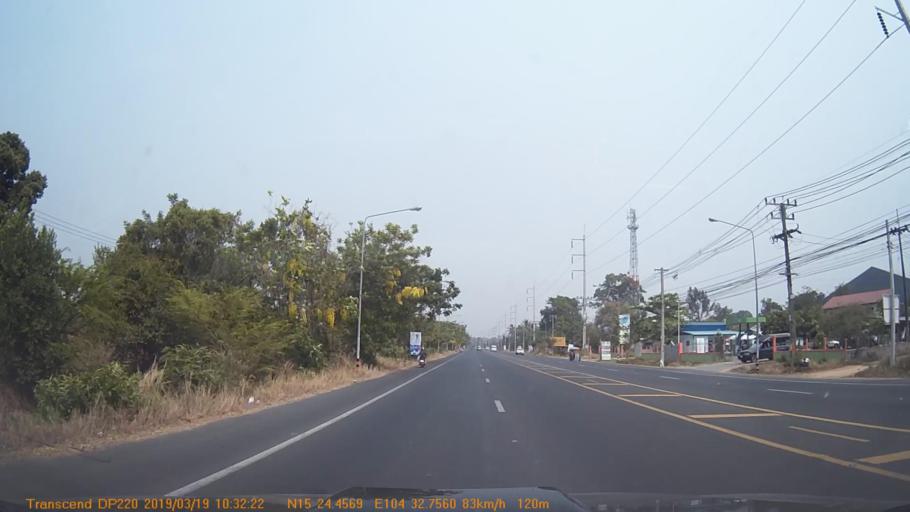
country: TH
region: Changwat Ubon Ratchathani
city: Khueang Nai
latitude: 15.4079
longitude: 104.5458
